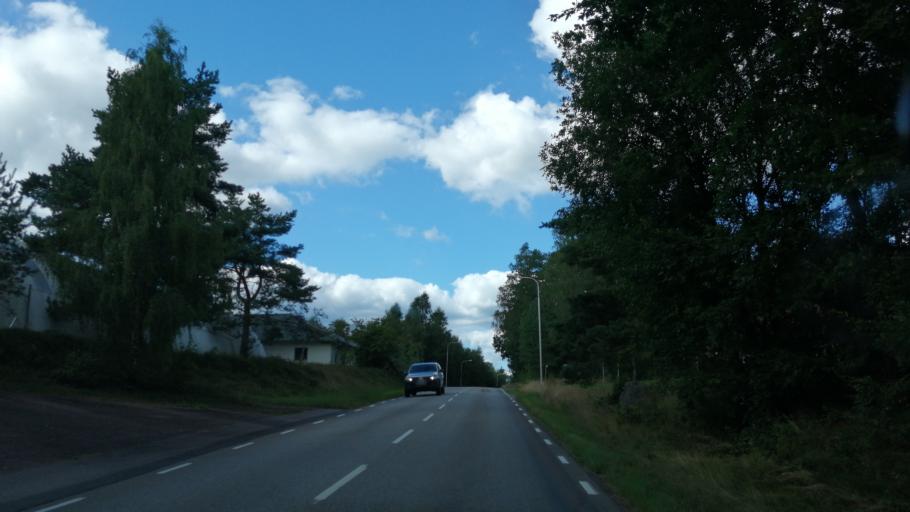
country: SE
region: Joenkoeping
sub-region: Varnamo Kommun
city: Bredaryd
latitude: 57.0877
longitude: 13.6860
